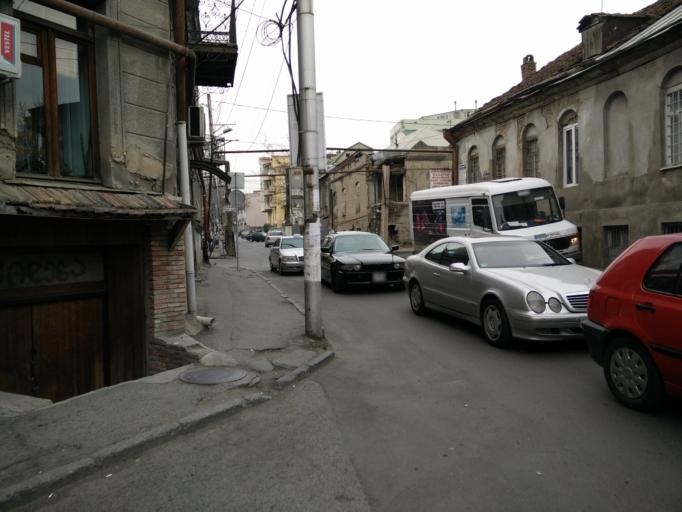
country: GE
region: T'bilisi
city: Tbilisi
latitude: 41.6941
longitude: 44.8146
